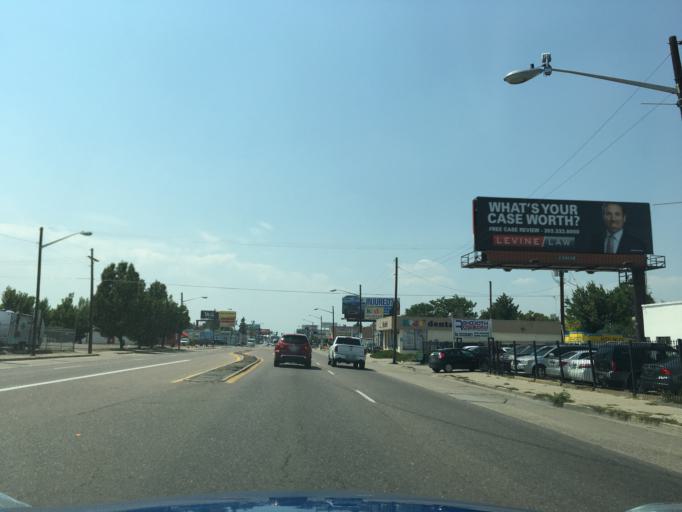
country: US
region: Colorado
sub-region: Arapahoe County
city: Glendale
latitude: 39.7402
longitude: -104.8950
